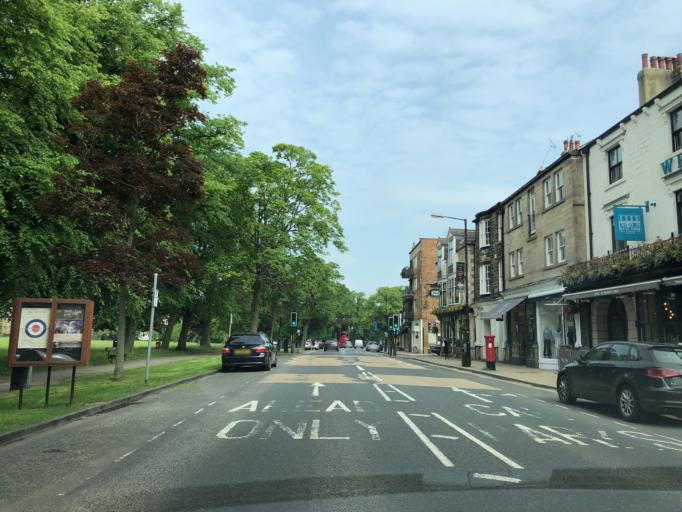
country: GB
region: England
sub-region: North Yorkshire
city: Harrogate
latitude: 53.9883
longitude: -1.5401
